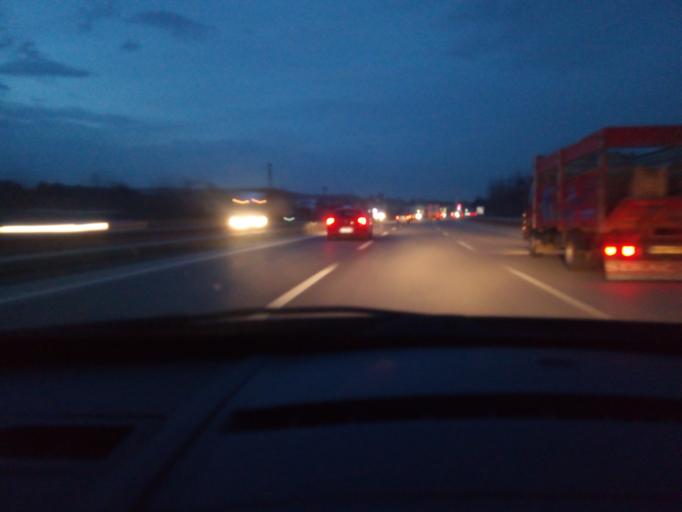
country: TR
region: Balikesir
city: Susurluk
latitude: 39.9617
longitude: 28.1704
